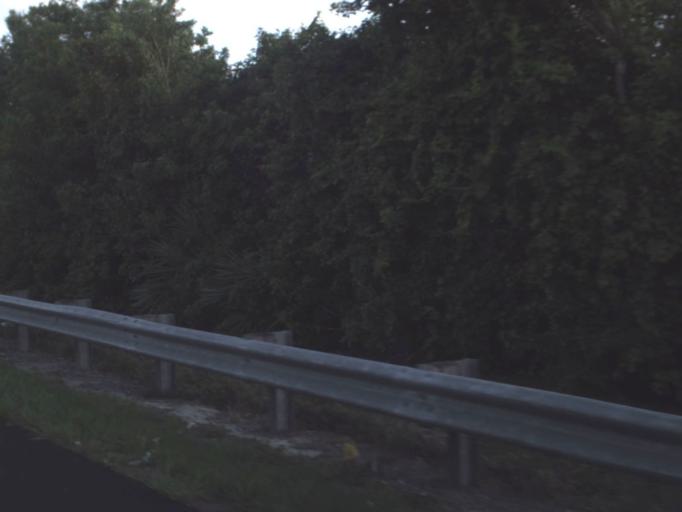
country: US
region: Florida
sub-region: Brevard County
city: South Patrick Shores
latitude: 28.2477
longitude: -80.6805
